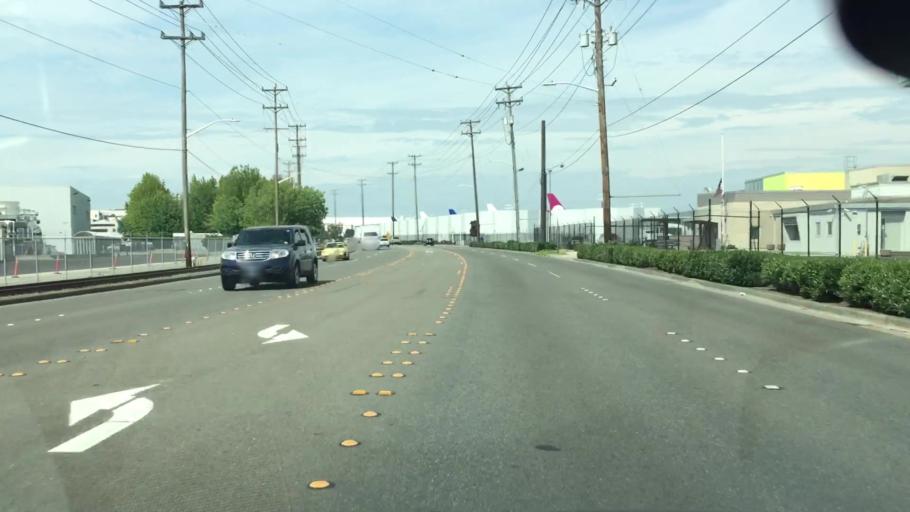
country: US
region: Washington
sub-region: King County
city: Boulevard Park
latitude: 47.5284
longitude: -122.3043
